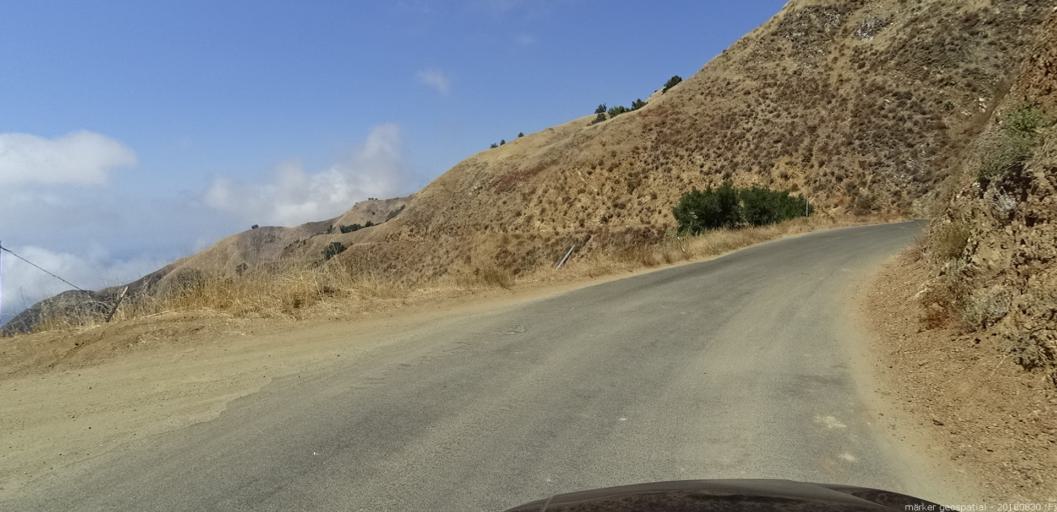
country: US
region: California
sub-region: Monterey County
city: Greenfield
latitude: 35.9969
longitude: -121.4599
